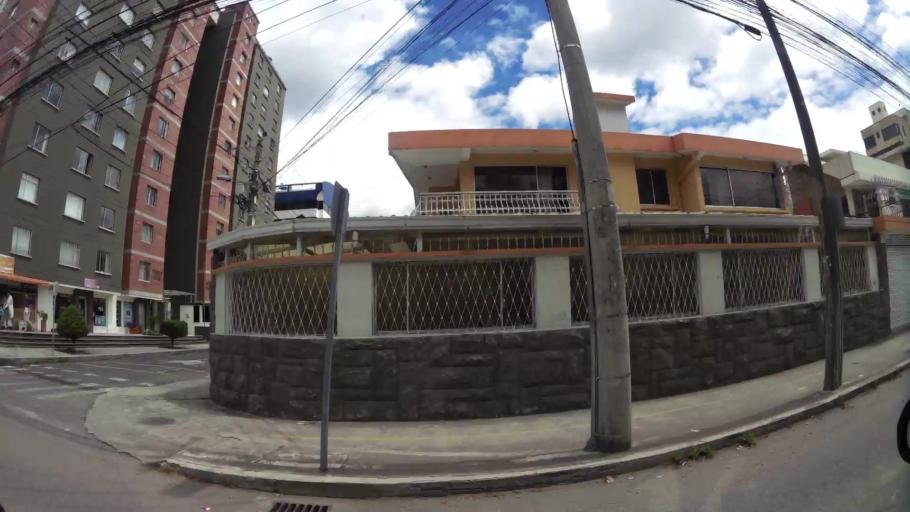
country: EC
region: Pichincha
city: Quito
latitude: -0.1707
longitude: -78.4828
